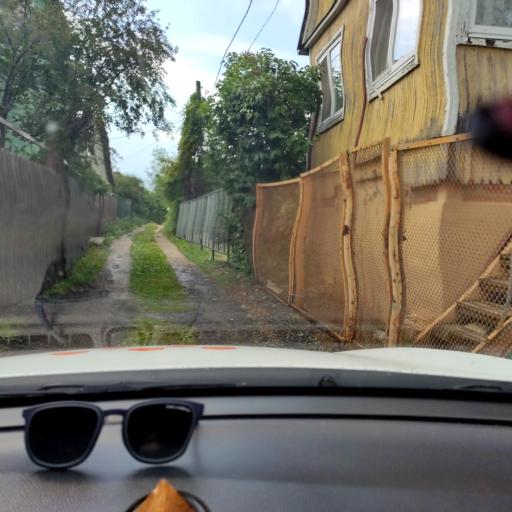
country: RU
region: Tatarstan
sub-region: Zelenodol'skiy Rayon
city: Vasil'yevo
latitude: 55.8220
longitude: 48.7273
